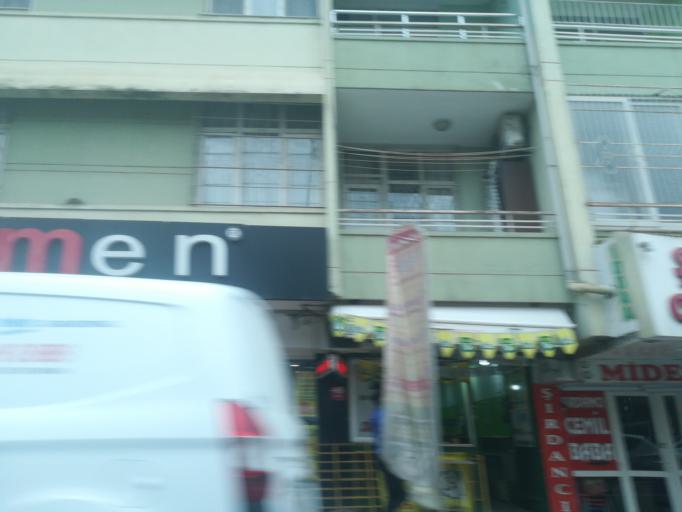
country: TR
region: Adana
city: Adana
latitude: 37.0348
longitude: 35.3078
